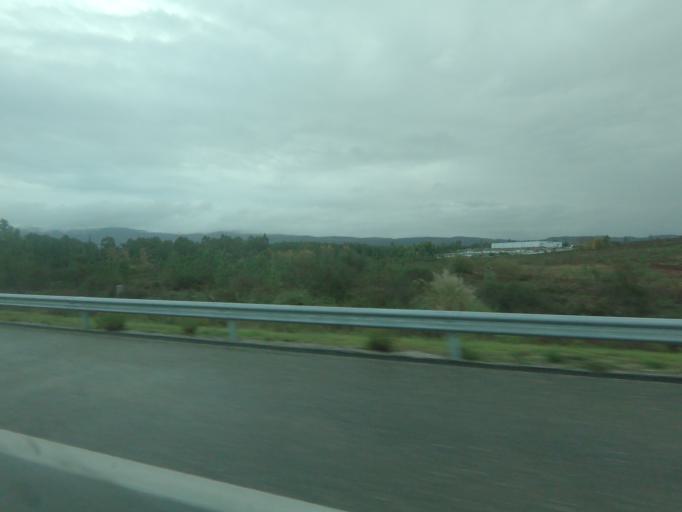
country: PT
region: Viana do Castelo
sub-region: Valenca
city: Valenza
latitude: 41.9714
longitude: -8.6646
